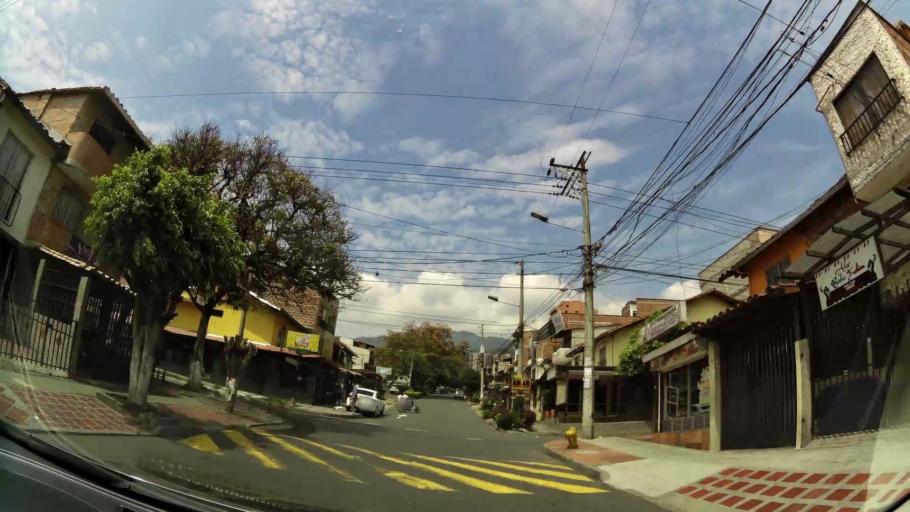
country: CO
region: Antioquia
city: Bello
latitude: 6.3196
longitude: -75.5603
